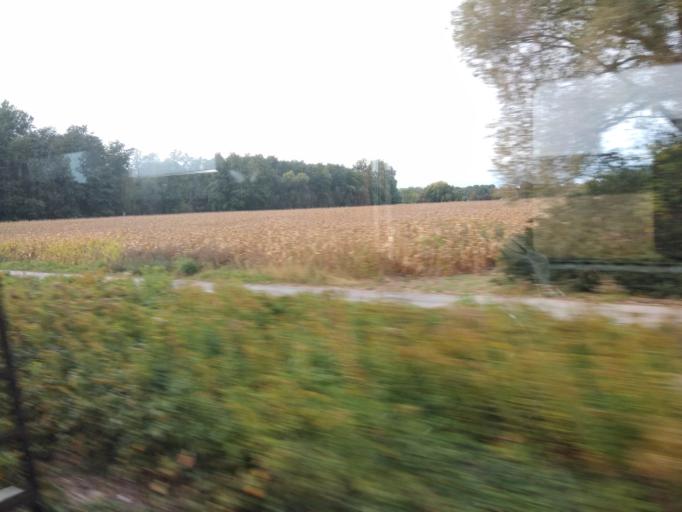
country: DE
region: Baden-Wuerttemberg
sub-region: Karlsruhe Region
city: Weingarten
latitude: 49.0484
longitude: 8.5111
